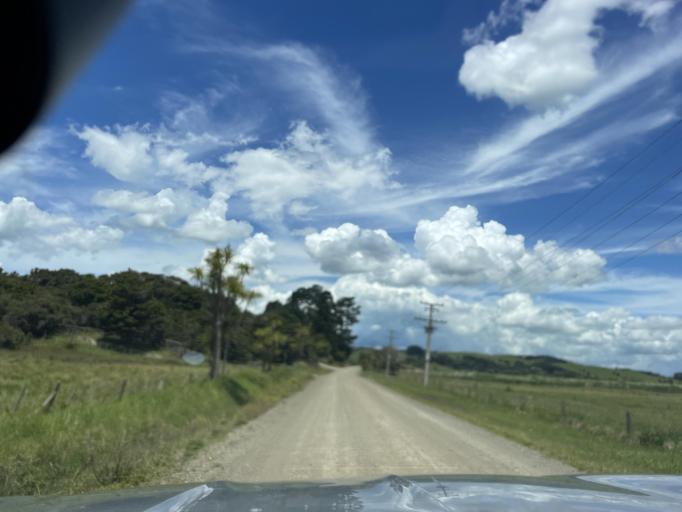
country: NZ
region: Northland
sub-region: Kaipara District
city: Dargaville
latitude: -35.8947
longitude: 173.9121
